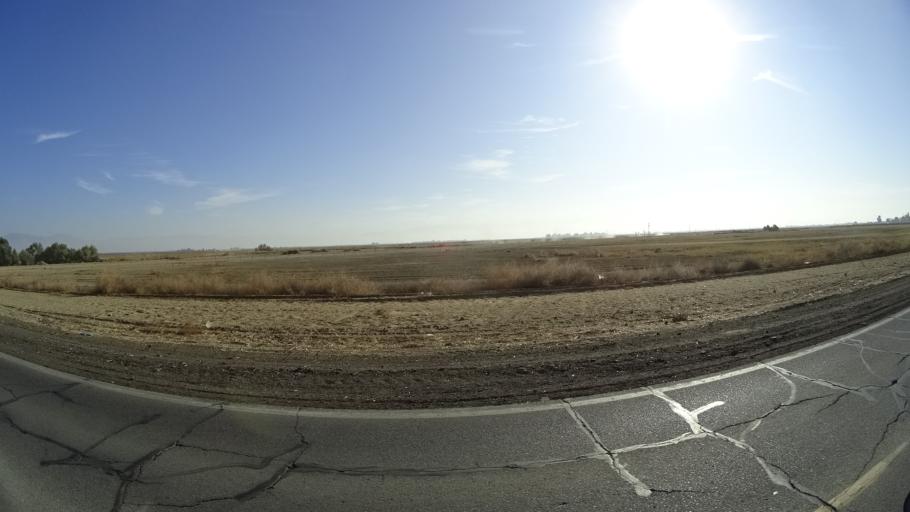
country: US
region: California
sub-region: Kern County
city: Greenfield
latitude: 35.2960
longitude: -118.9643
